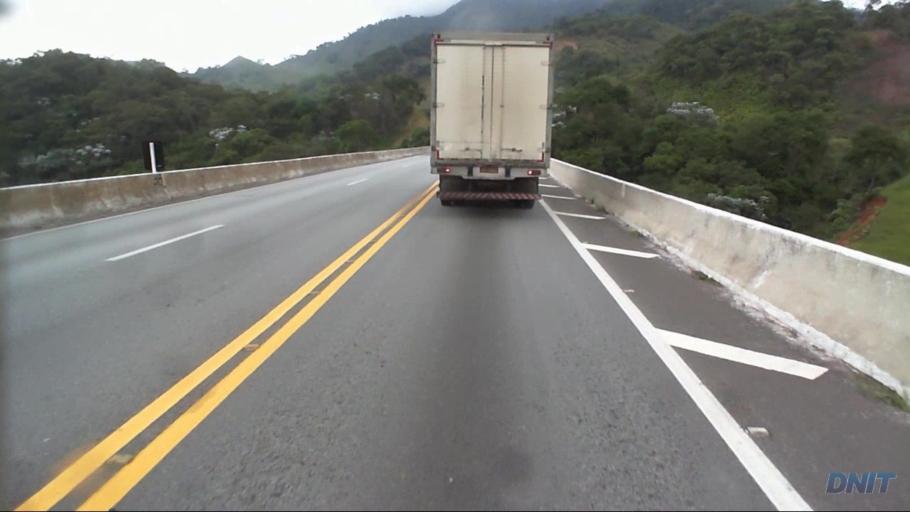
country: BR
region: Minas Gerais
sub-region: Nova Era
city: Nova Era
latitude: -19.6552
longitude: -42.9562
